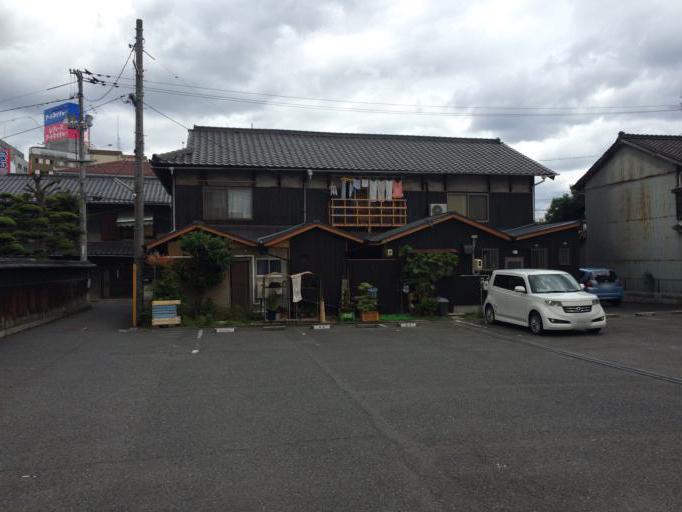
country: JP
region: Okayama
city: Kurashiki
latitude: 34.5999
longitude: 133.7657
